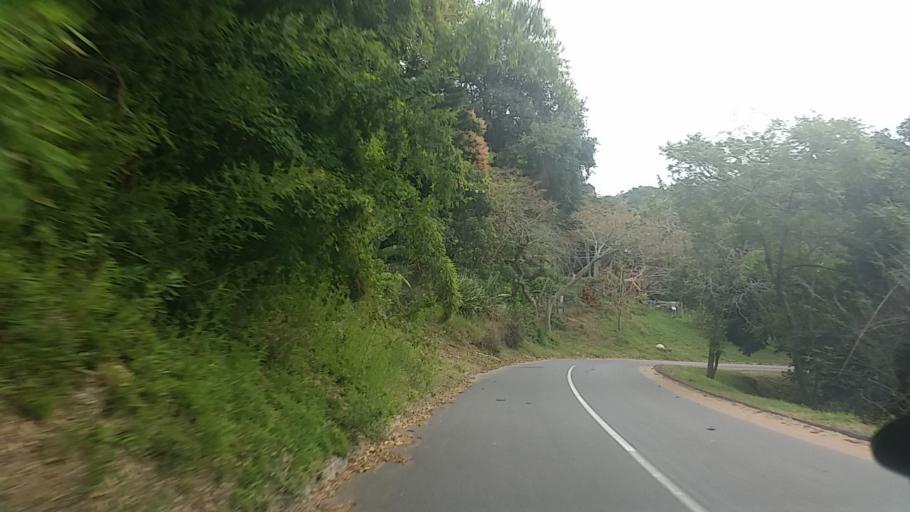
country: ZA
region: KwaZulu-Natal
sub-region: eThekwini Metropolitan Municipality
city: Berea
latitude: -29.8410
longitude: 30.9333
